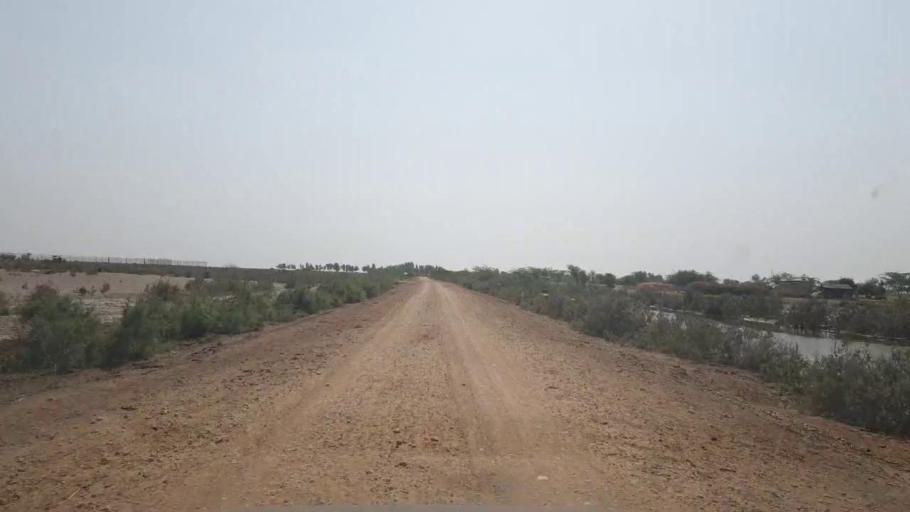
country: PK
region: Sindh
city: Jati
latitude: 24.3838
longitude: 68.6001
